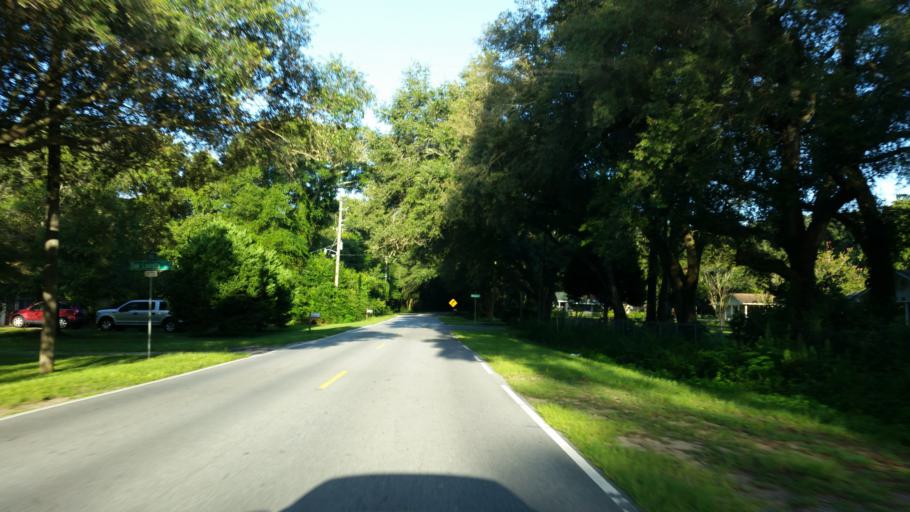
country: US
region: Florida
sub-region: Escambia County
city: Bellview
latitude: 30.4483
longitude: -87.3212
